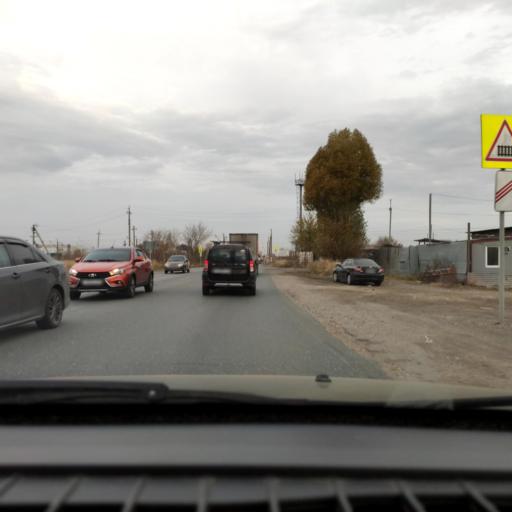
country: RU
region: Samara
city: Tol'yatti
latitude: 53.5606
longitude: 49.3580
